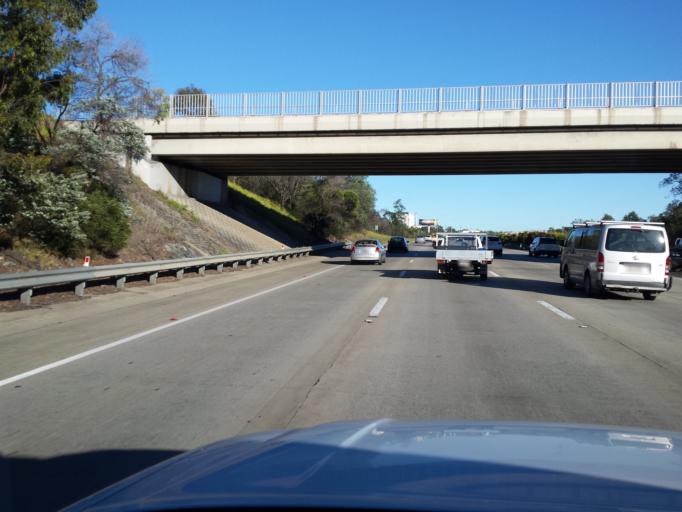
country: AU
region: Queensland
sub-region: Gold Coast
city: Ormeau Hills
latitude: -27.7587
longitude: 153.2425
